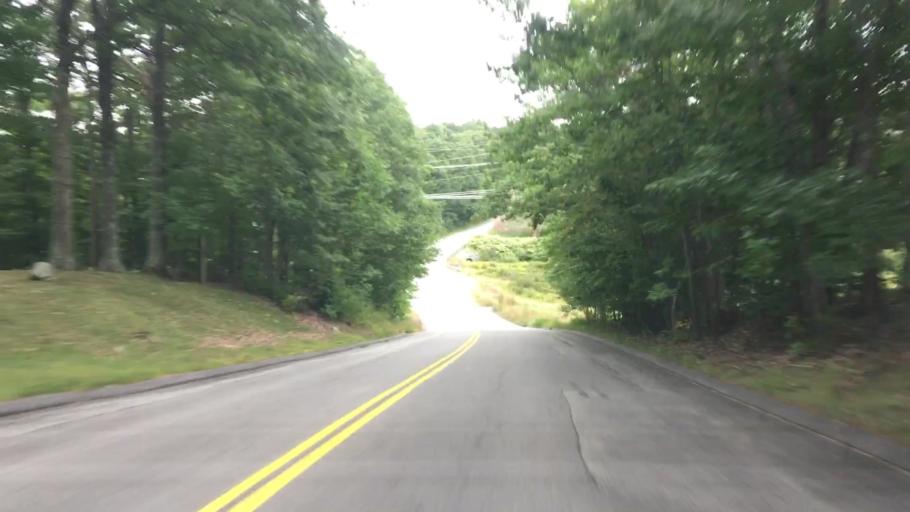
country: US
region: Maine
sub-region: Cumberland County
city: New Gloucester
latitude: 43.9089
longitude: -70.2235
